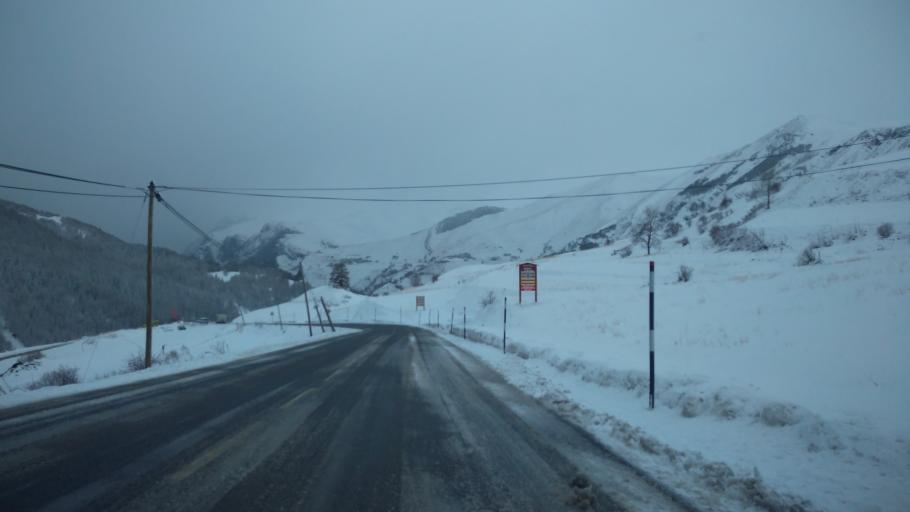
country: FR
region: Rhone-Alpes
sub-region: Departement de la Savoie
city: Valloire
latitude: 45.0412
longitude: 6.3446
